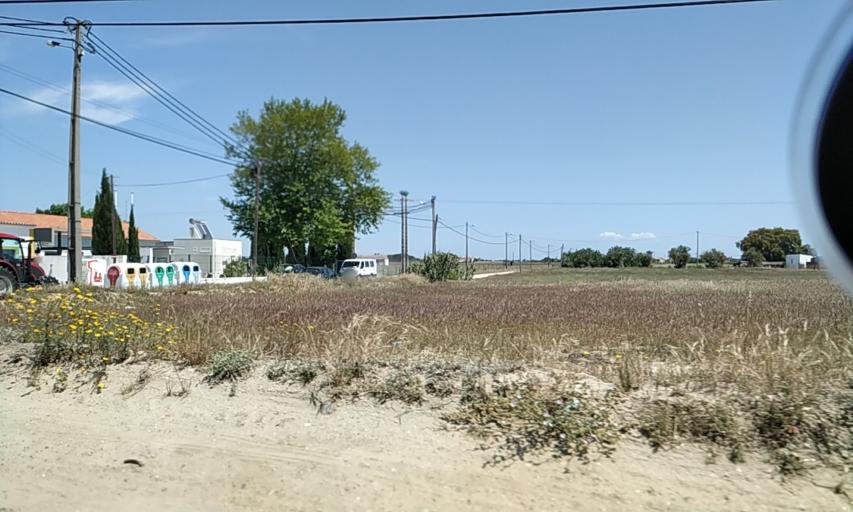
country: PT
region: Santarem
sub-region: Benavente
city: Poceirao
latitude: 38.6657
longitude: -8.7373
